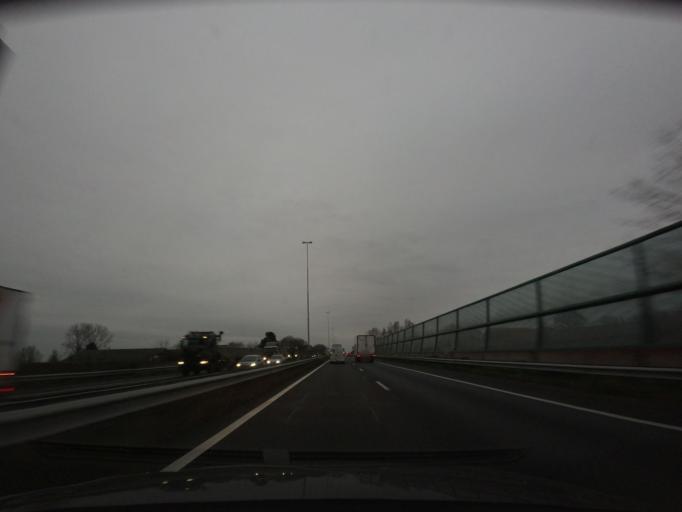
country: NL
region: North Brabant
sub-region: Gemeente Woudrichem
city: Almkerk
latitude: 51.7572
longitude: 4.9257
